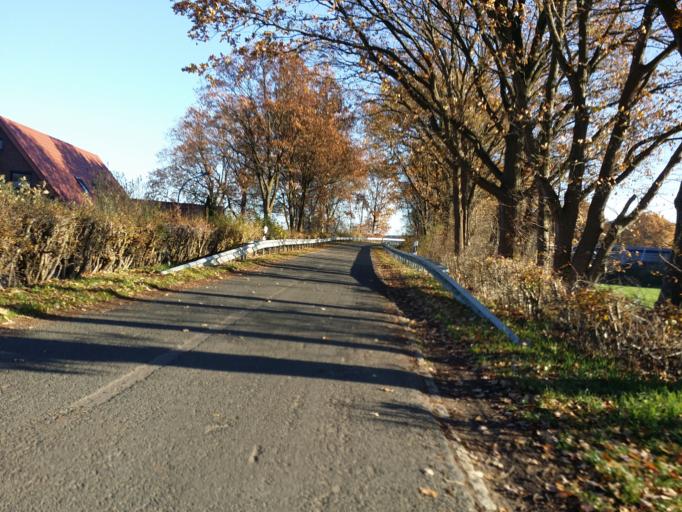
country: DE
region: Lower Saxony
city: Ottersberg
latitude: 53.0617
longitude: 9.0988
